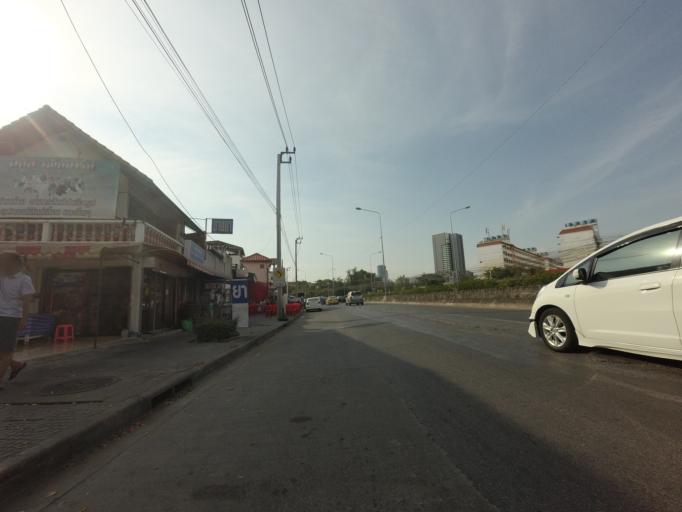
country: TH
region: Bangkok
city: Bang Kapi
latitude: 13.7548
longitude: 100.6294
